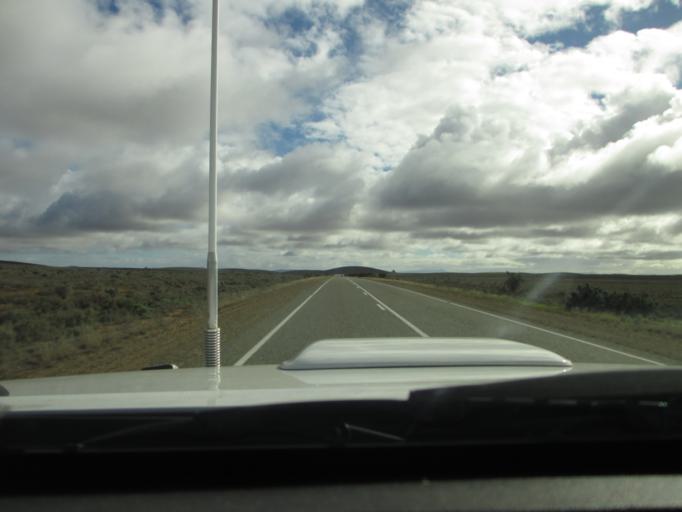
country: AU
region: South Australia
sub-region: Flinders Ranges
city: Quorn
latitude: -32.1763
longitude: 138.5379
